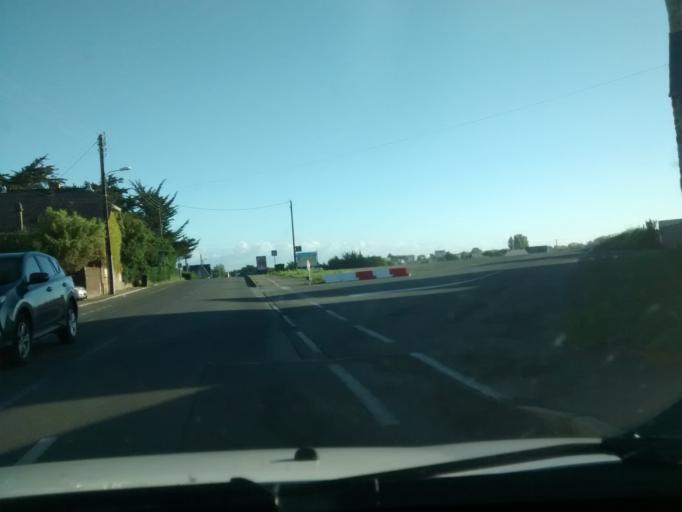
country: FR
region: Brittany
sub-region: Departement d'Ille-et-Vilaine
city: Saint-Malo
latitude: 48.6730
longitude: -1.9815
